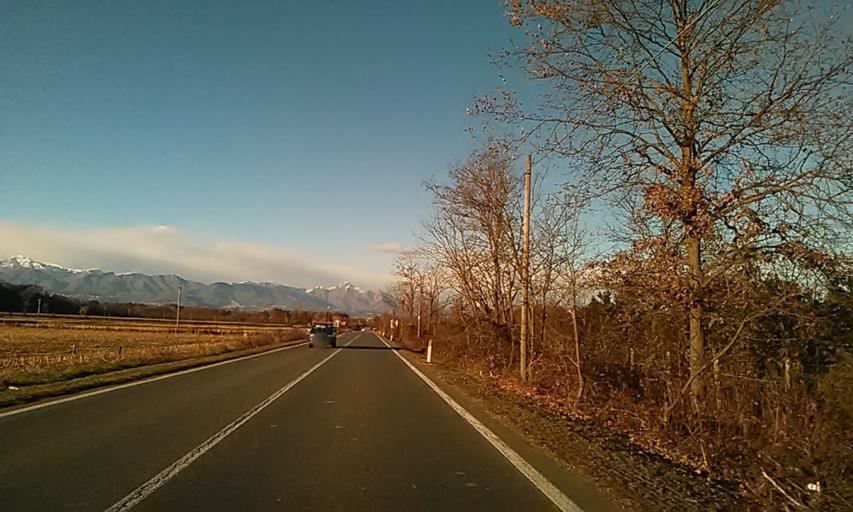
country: IT
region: Piedmont
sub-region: Provincia di Biella
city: Gifflenga
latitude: 45.4807
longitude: 8.2180
